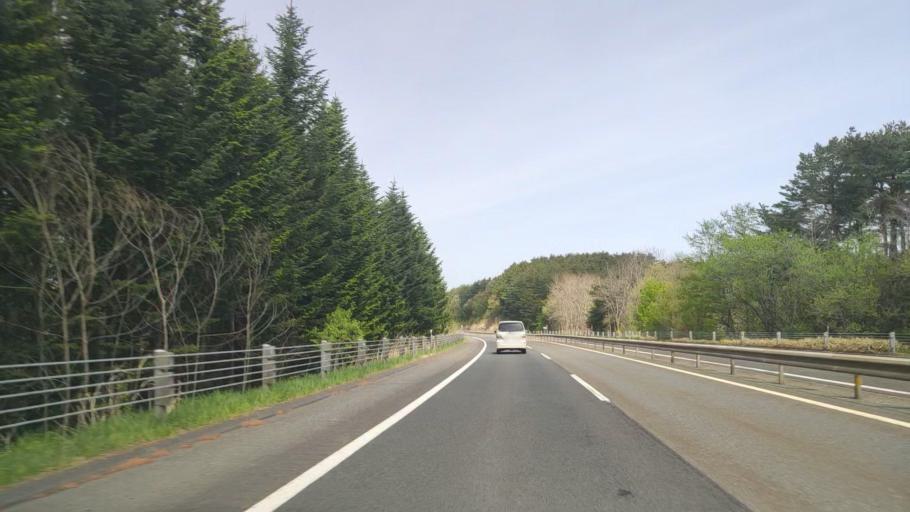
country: JP
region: Aomori
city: Hachinohe
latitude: 40.4695
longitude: 141.4614
